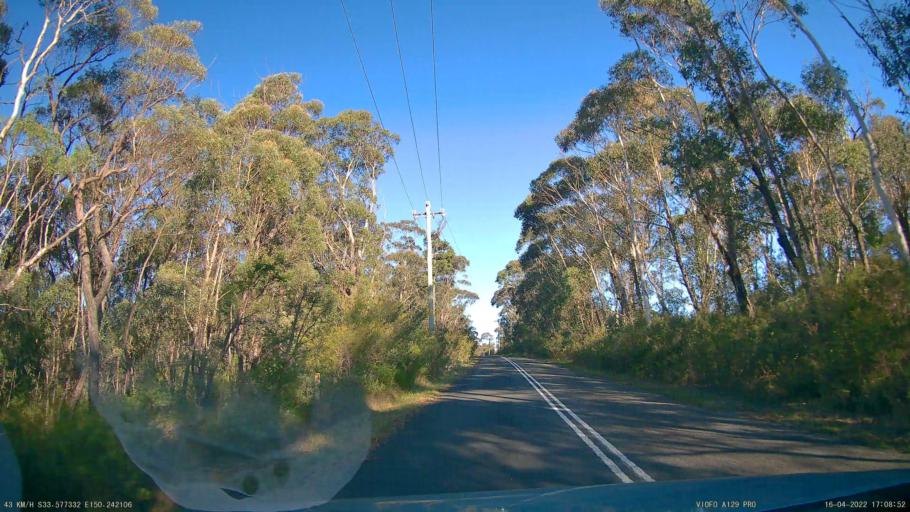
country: AU
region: New South Wales
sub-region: Blue Mountains Municipality
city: Blackheath
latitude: -33.5774
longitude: 150.2422
